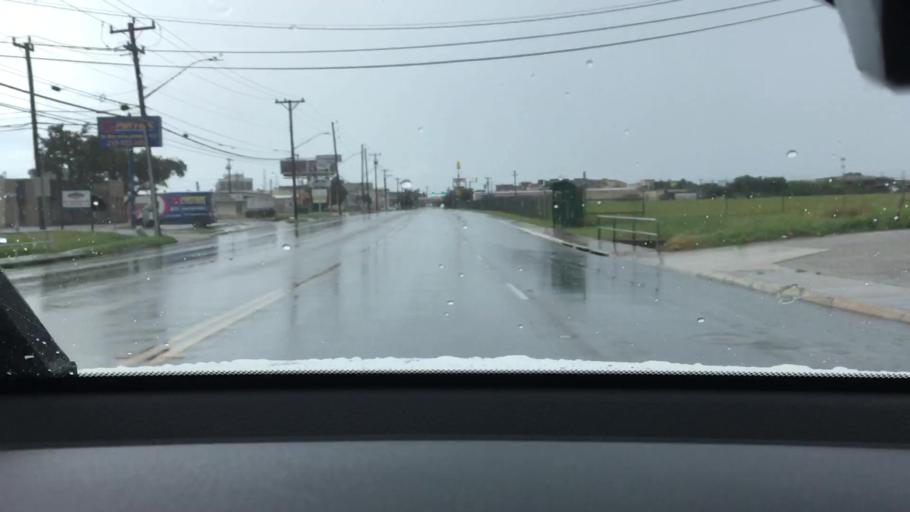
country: US
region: Texas
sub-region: Bexar County
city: Alamo Heights
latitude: 29.5234
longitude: -98.4580
